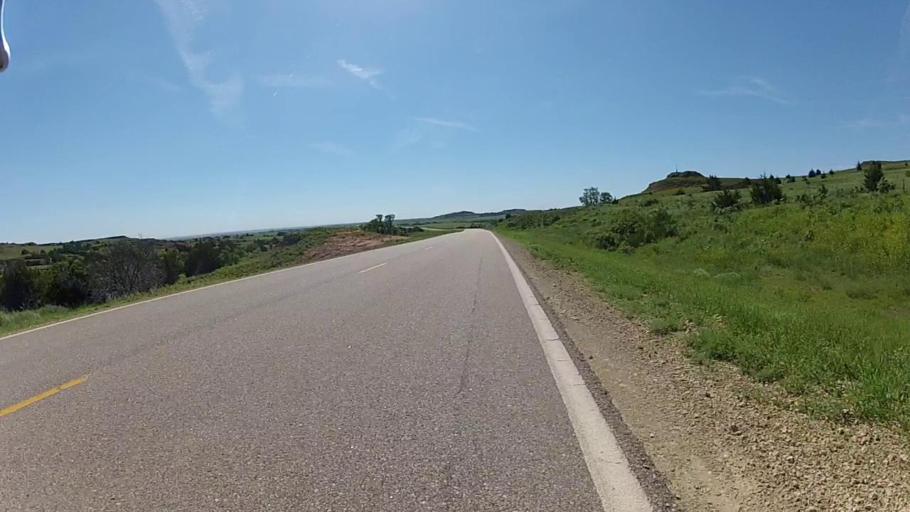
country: US
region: Kansas
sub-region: Barber County
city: Medicine Lodge
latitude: 37.2766
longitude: -98.7344
